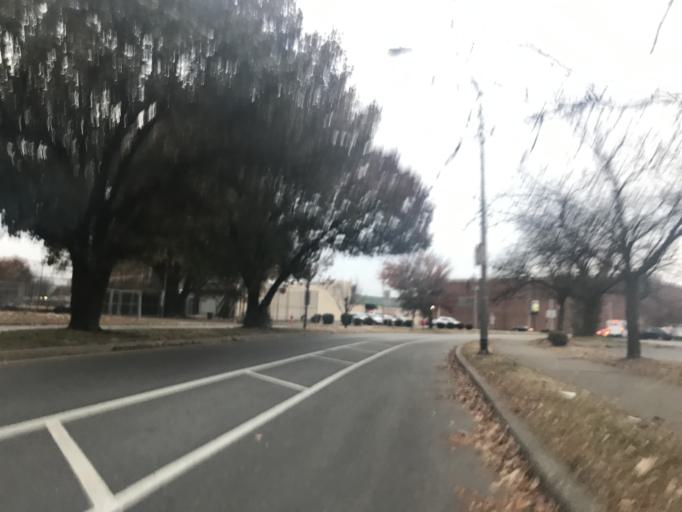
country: US
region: Kentucky
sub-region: Jefferson County
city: Louisville
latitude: 38.2488
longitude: -85.7721
